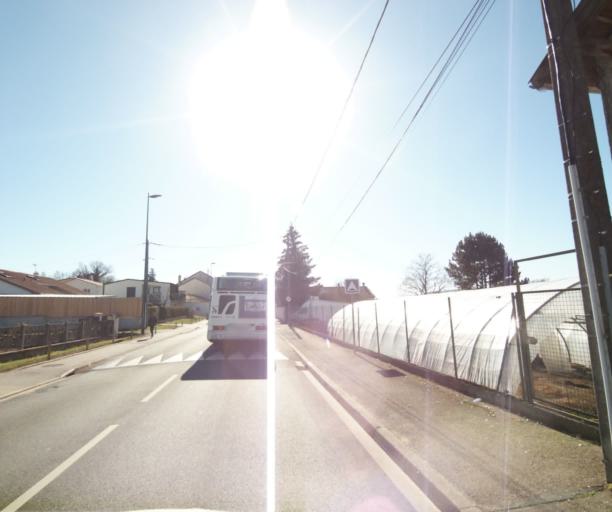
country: FR
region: Lorraine
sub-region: Departement de Meurthe-et-Moselle
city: Heillecourt
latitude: 48.6611
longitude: 6.2070
